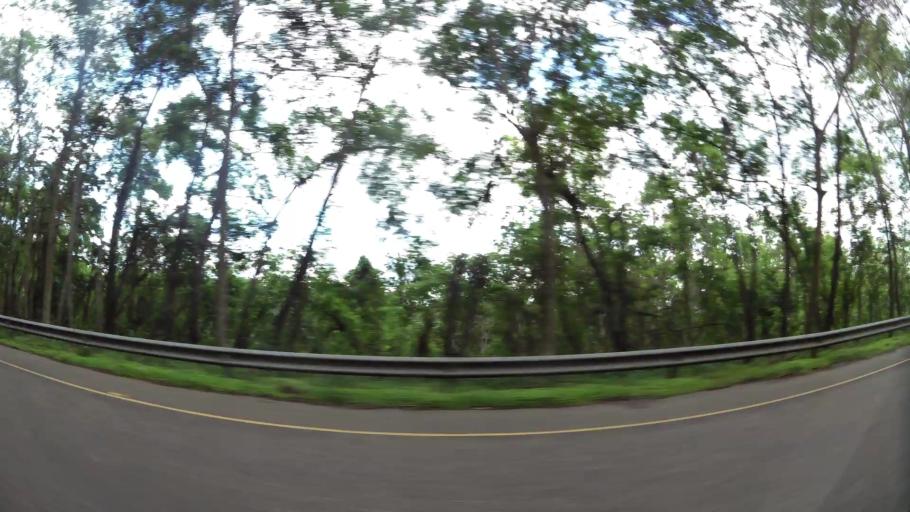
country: DO
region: Monsenor Nouel
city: Sabana del Puerto
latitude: 19.0900
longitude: -70.4376
